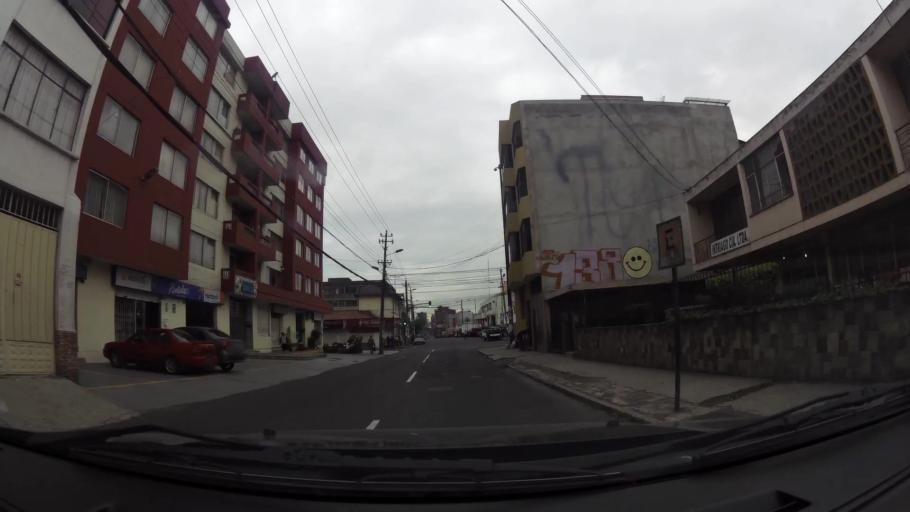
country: EC
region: Pichincha
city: Quito
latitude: -0.1992
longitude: -78.4988
